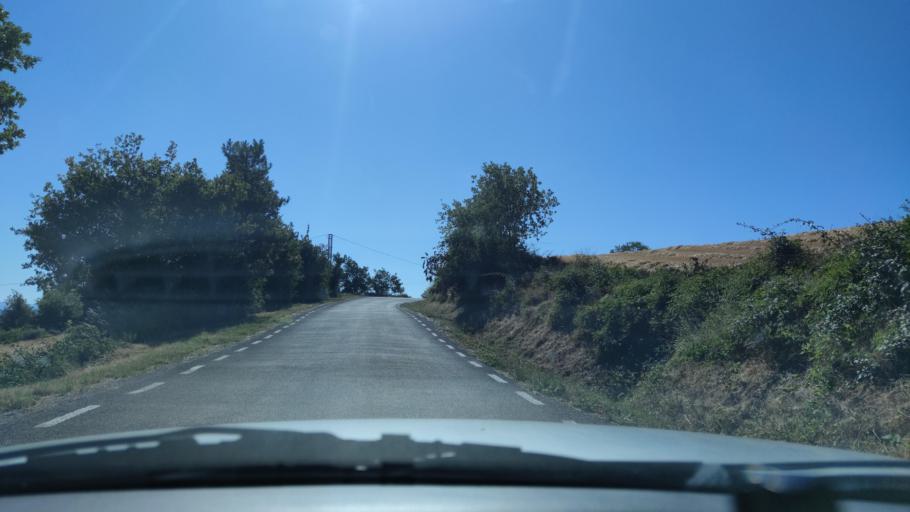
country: ES
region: Catalonia
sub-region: Provincia de Lleida
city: Solsona
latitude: 41.9556
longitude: 1.4925
